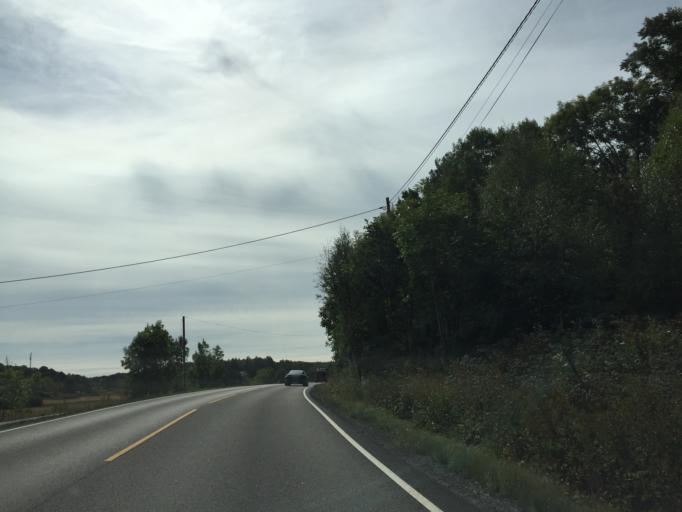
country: NO
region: Ostfold
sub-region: Fredrikstad
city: Fredrikstad
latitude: 59.1756
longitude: 10.9326
